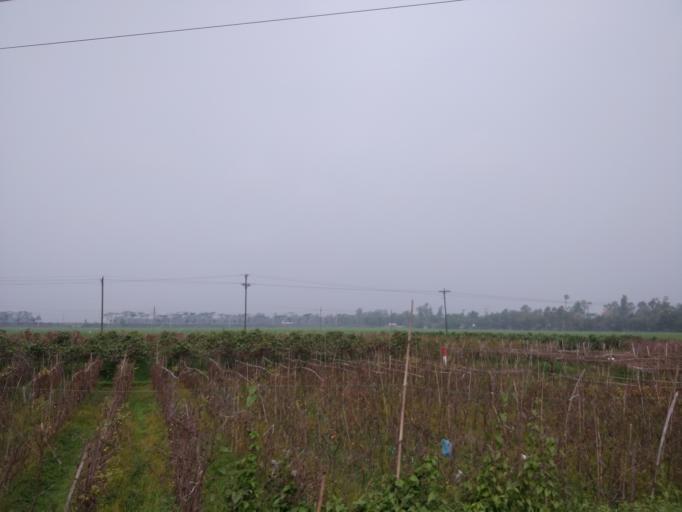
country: BD
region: Sylhet
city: Habiganj
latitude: 24.1654
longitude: 91.3539
